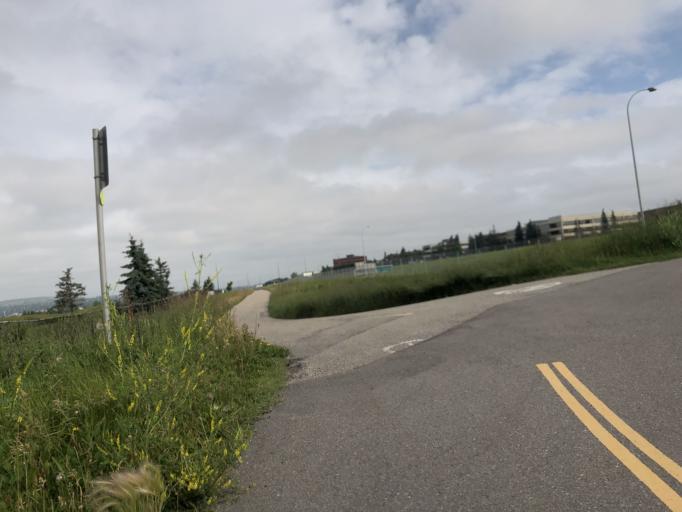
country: CA
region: Alberta
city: Calgary
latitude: 51.0749
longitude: -114.0282
